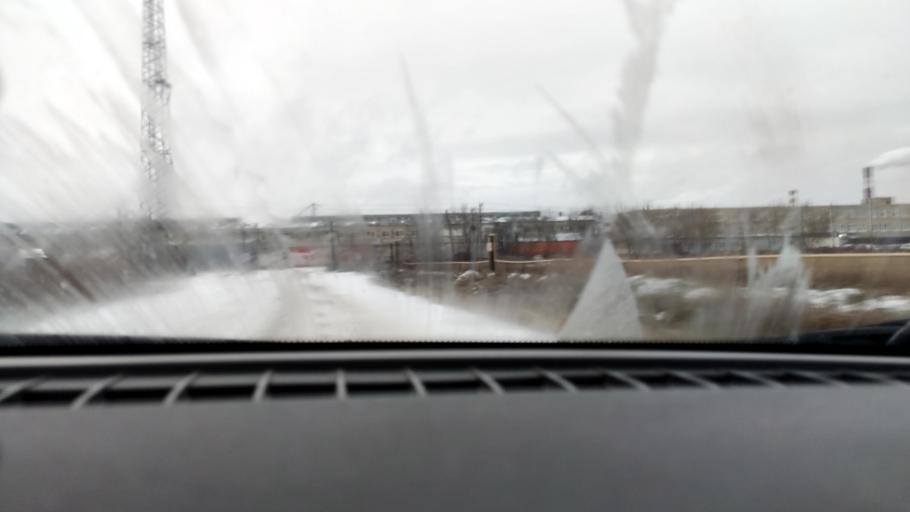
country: RU
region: Perm
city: Kondratovo
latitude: 57.9246
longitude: 56.1677
